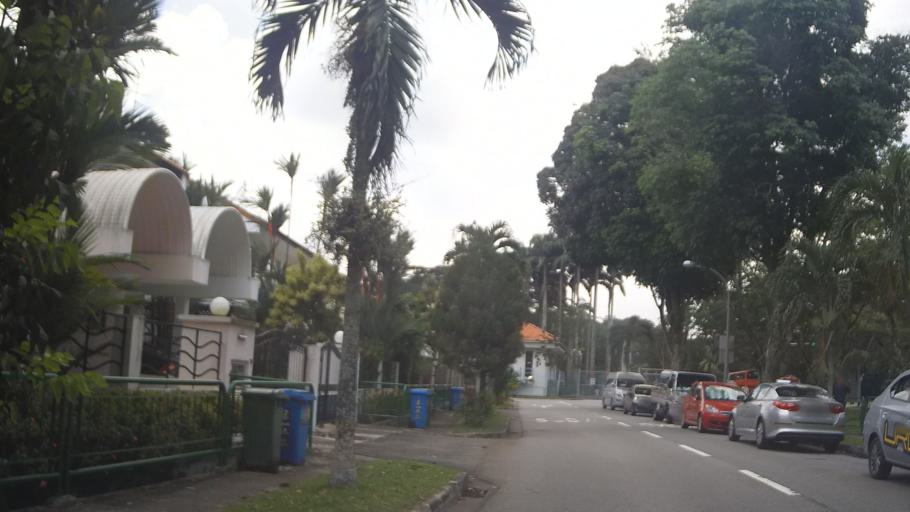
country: MY
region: Johor
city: Kampung Pasir Gudang Baru
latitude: 1.3912
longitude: 103.8556
